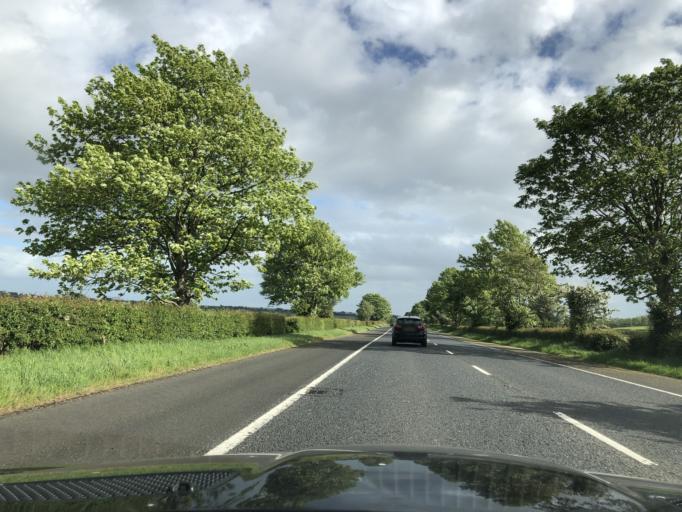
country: GB
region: Northern Ireland
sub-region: Ballymoney District
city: Ballymoney
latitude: 55.0985
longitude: -6.5364
